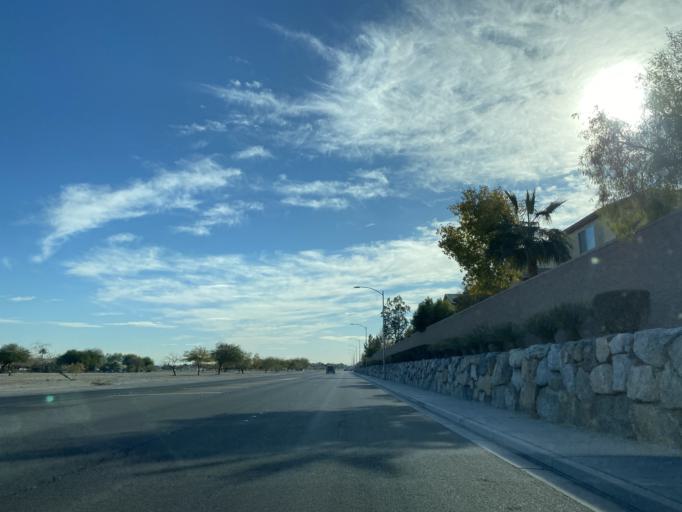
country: US
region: Nevada
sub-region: Clark County
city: North Las Vegas
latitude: 36.3087
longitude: -115.2423
